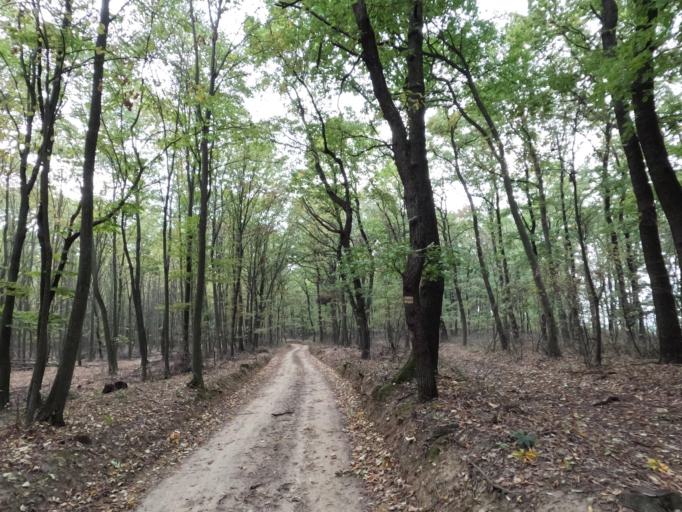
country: HU
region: Tolna
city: Szentgalpuszta
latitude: 46.3195
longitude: 18.6326
